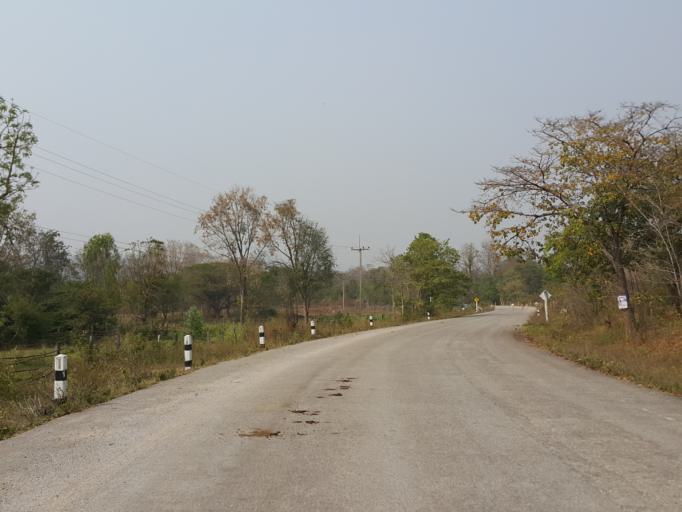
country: TH
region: Lampang
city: Mae Phrik
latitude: 17.4923
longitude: 99.0876
